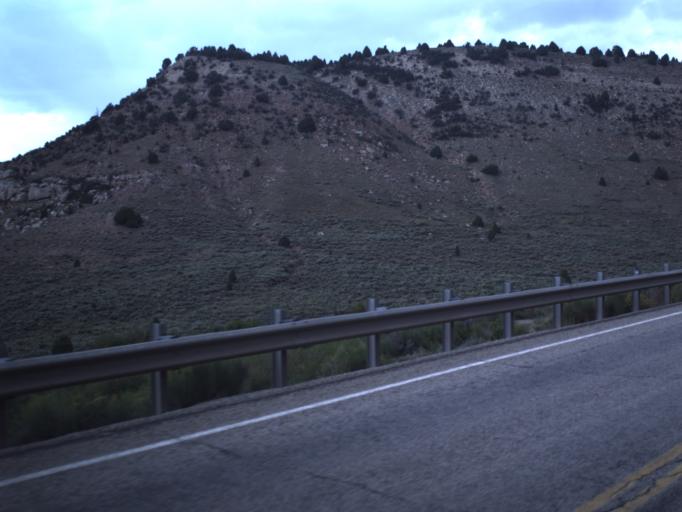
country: US
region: Utah
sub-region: Carbon County
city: Helper
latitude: 39.8287
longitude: -110.7883
